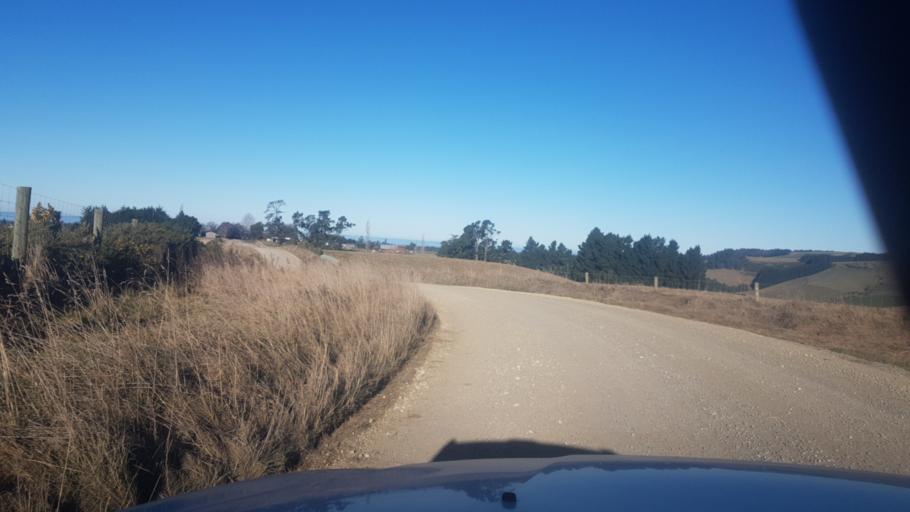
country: NZ
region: Canterbury
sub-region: Timaru District
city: Pleasant Point
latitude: -44.3697
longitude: 171.0729
